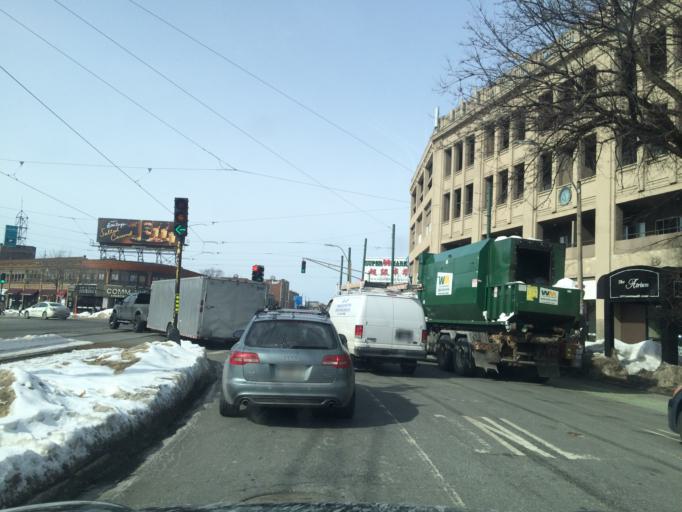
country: US
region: Massachusetts
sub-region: Norfolk County
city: Brookline
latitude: 42.3522
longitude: -71.1241
